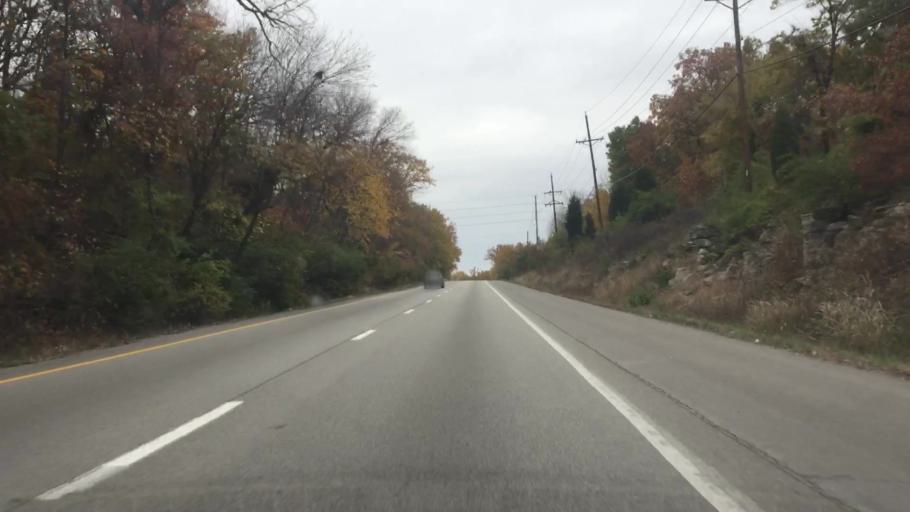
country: US
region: Missouri
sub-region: Jackson County
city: Raytown
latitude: 38.9698
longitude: -94.4371
